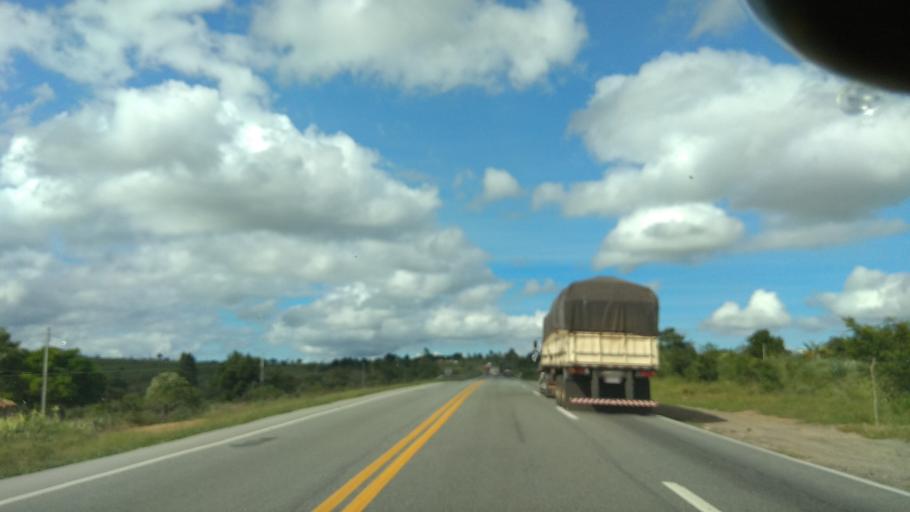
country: BR
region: Bahia
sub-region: Santa Ines
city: Santa Ines
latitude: -13.1078
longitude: -39.9757
